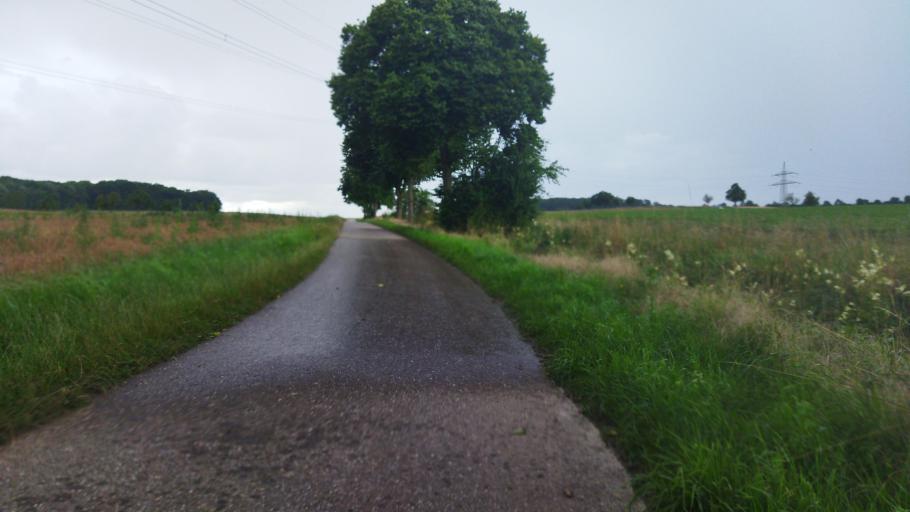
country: DE
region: Baden-Wuerttemberg
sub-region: Regierungsbezirk Stuttgart
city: Massenbachhausen
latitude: 49.2053
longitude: 9.0310
